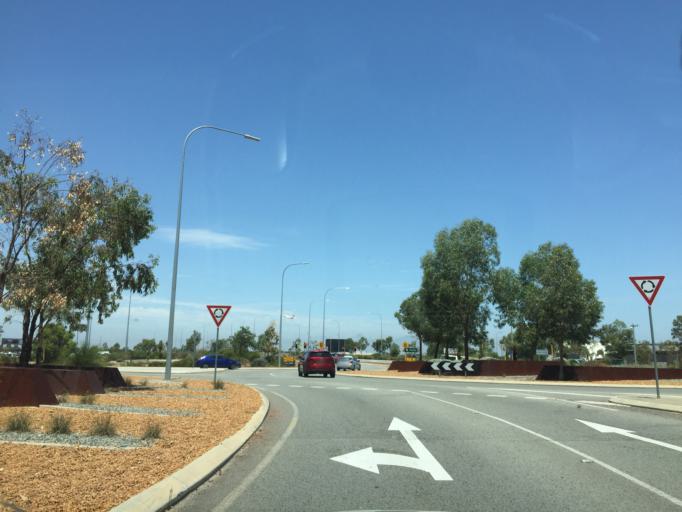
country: AU
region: Western Australia
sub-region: Belmont
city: Redcliffe
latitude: -31.9483
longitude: 115.9731
